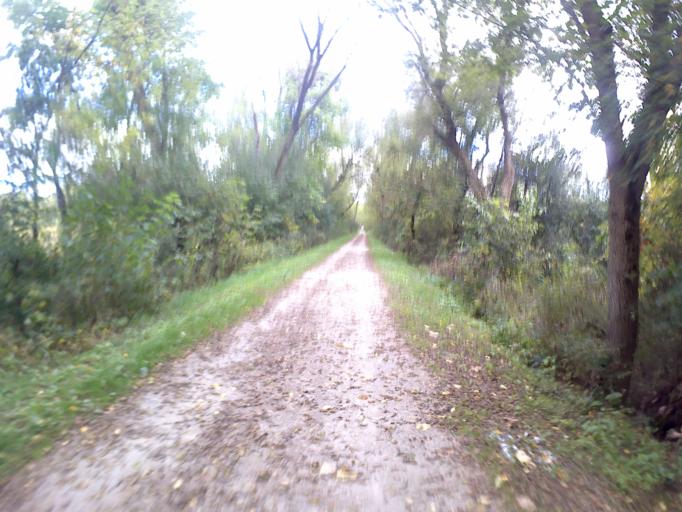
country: US
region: Illinois
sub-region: DuPage County
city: Wayne
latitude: 41.9458
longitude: -88.2358
